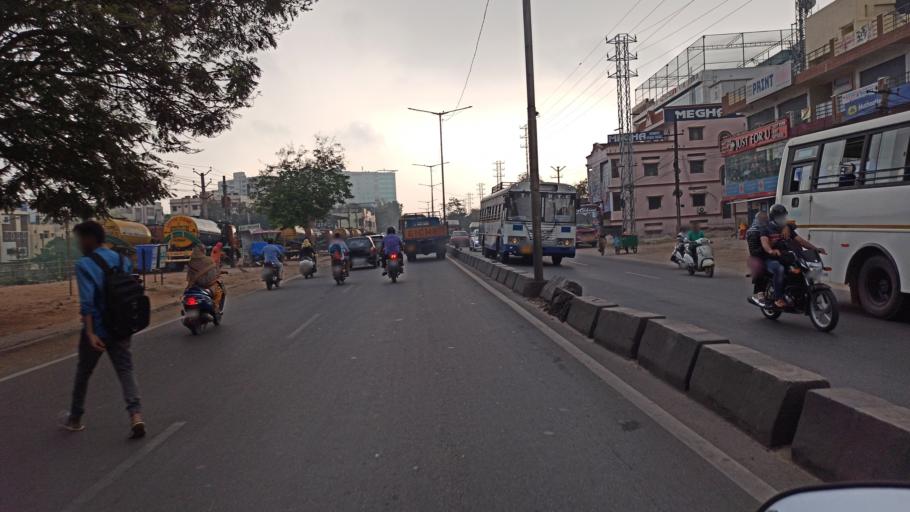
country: IN
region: Telangana
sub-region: Rangareddi
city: Uppal Kalan
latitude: 17.4006
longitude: 78.5408
